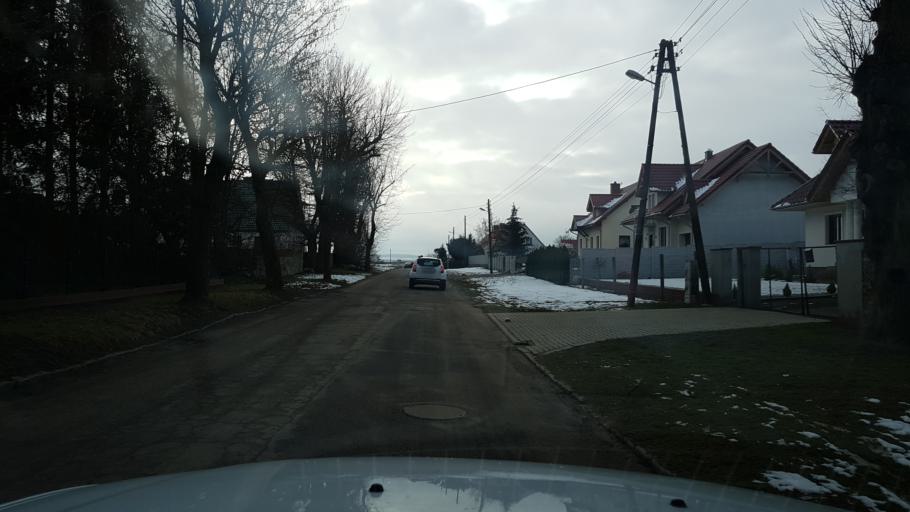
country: PL
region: West Pomeranian Voivodeship
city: Trzcinsko Zdroj
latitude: 52.9657
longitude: 14.6728
